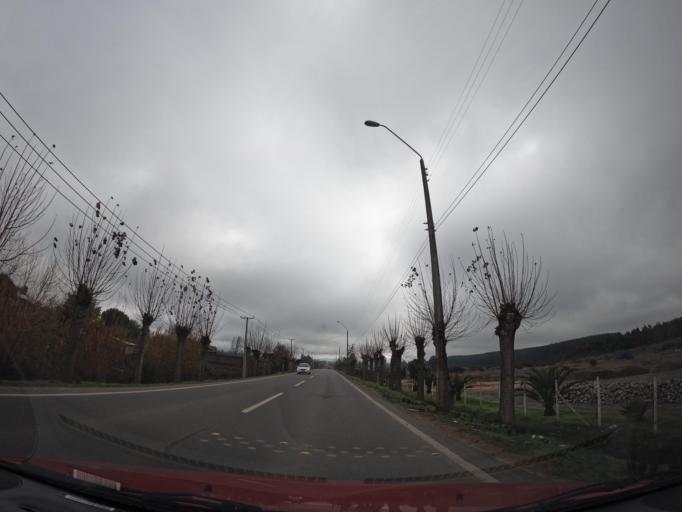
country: CL
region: Maule
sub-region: Provincia de Cauquenes
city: Cauquenes
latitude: -36.2733
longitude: -72.5424
